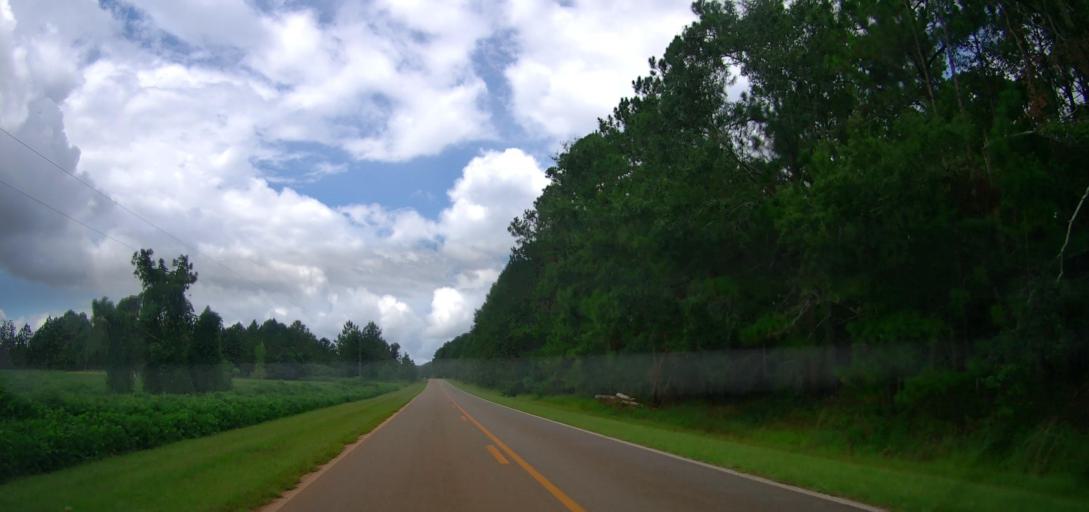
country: US
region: Georgia
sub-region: Pulaski County
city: Hawkinsville
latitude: 32.3395
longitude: -83.5473
